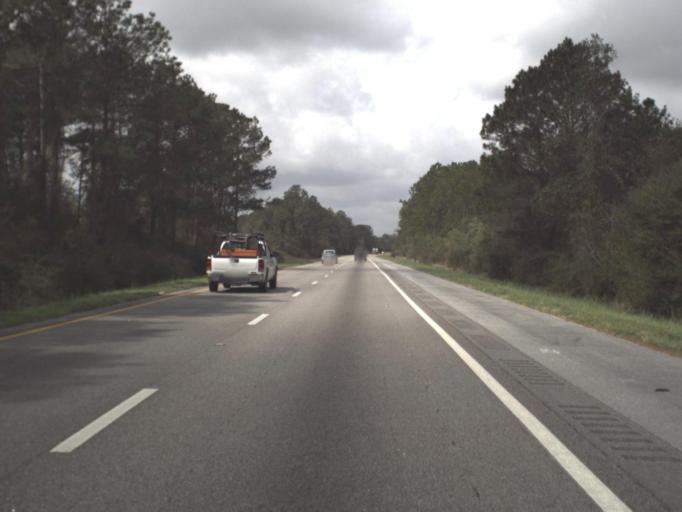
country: US
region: Florida
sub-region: Okaloosa County
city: Crestview
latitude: 30.7196
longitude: -86.4345
